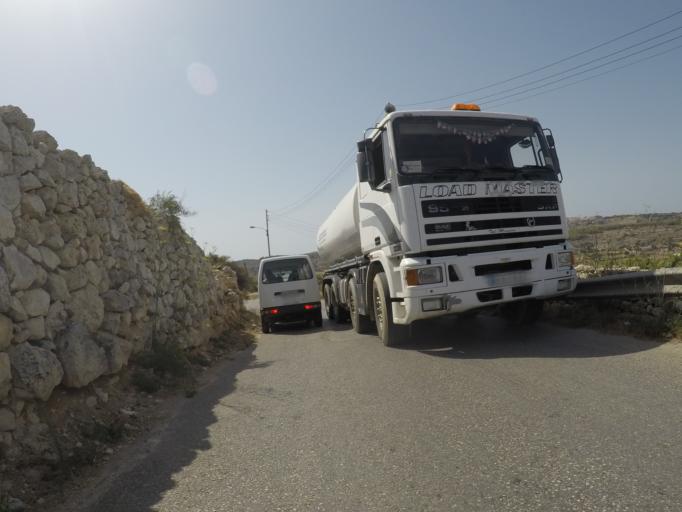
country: MT
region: L-Imgarr
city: Imgarr
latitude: 35.9378
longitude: 14.3796
